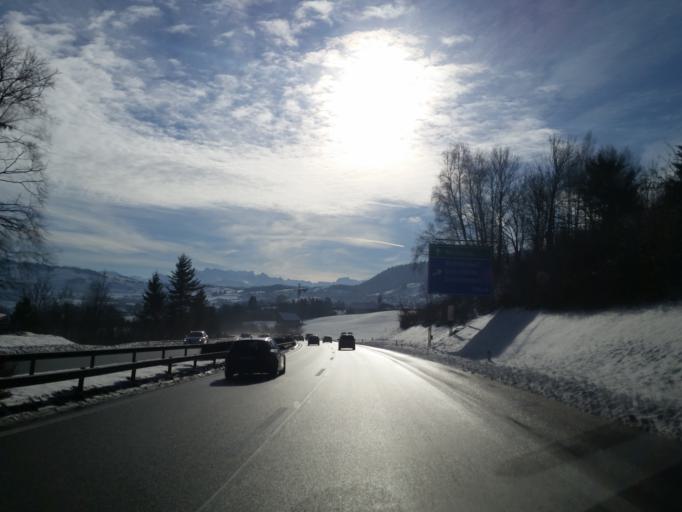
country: CH
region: Zurich
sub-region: Bezirk Horgen
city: Waedenswil / Eichweid
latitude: 47.2071
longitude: 8.6763
